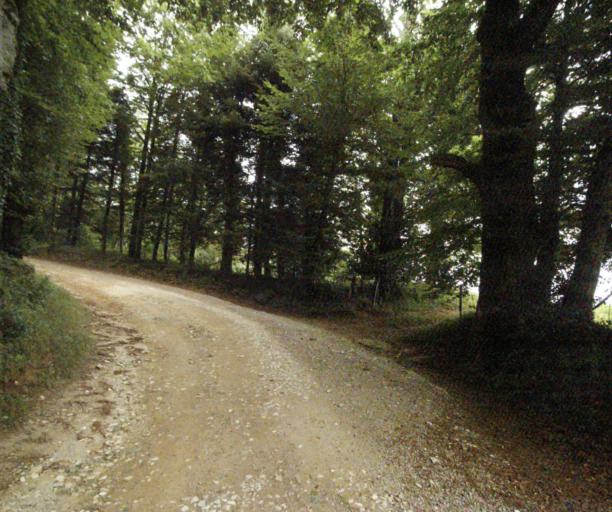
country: FR
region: Midi-Pyrenees
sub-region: Departement du Tarn
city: Soreze
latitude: 43.4215
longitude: 2.1041
